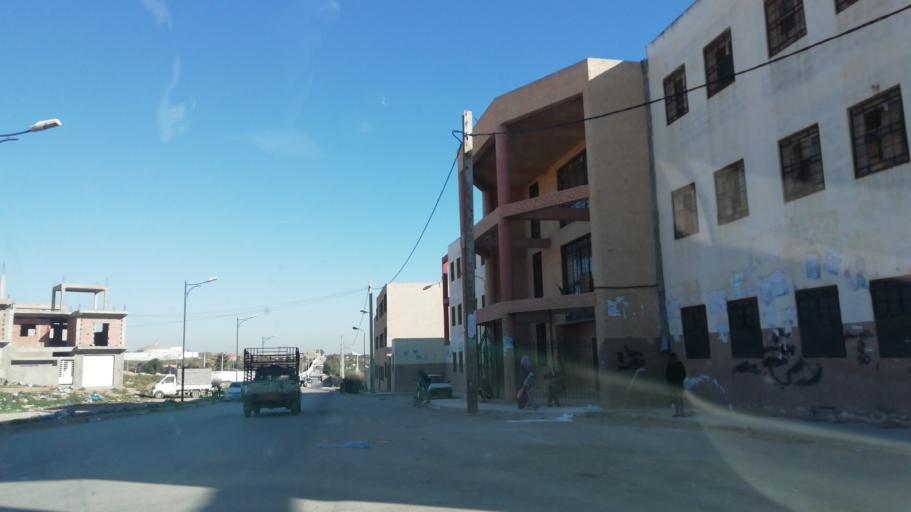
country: DZ
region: Oran
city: Bir el Djir
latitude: 35.7246
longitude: -0.5284
